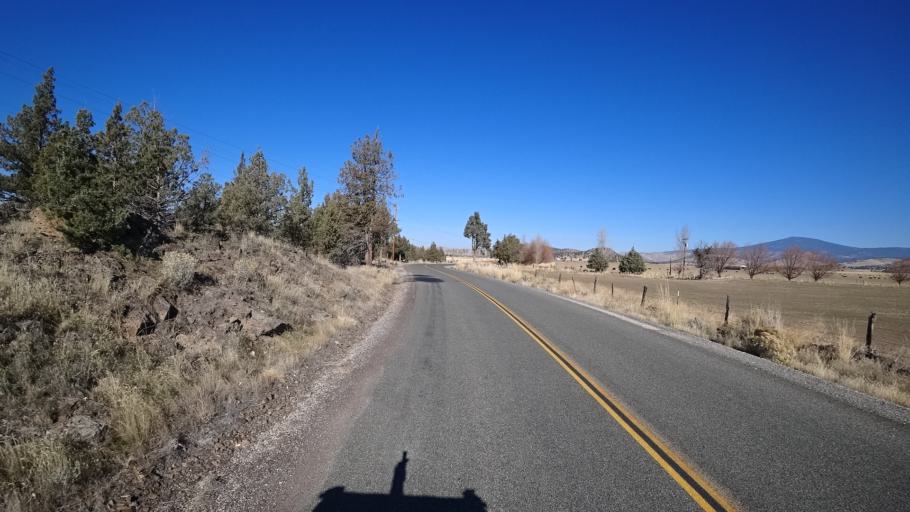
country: US
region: California
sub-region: Siskiyou County
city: Montague
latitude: 41.6732
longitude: -122.3695
